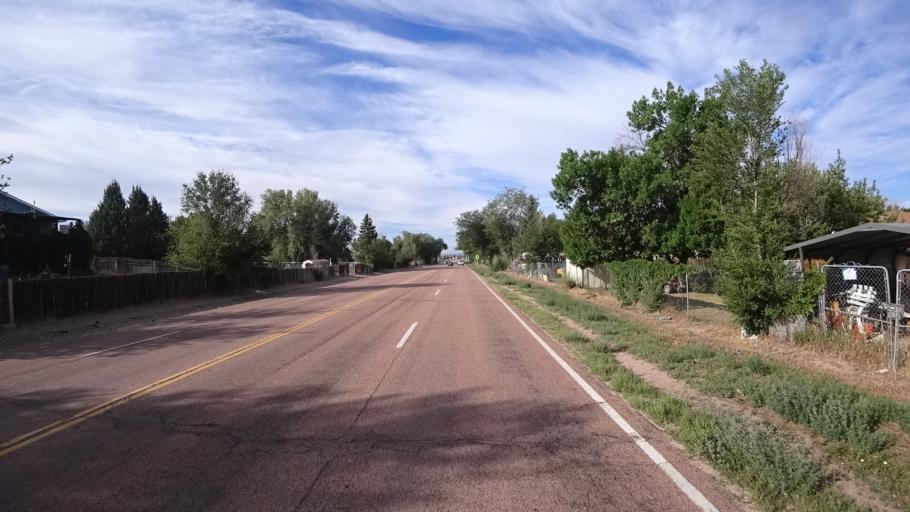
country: US
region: Colorado
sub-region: El Paso County
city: Security-Widefield
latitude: 38.7259
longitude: -104.6988
